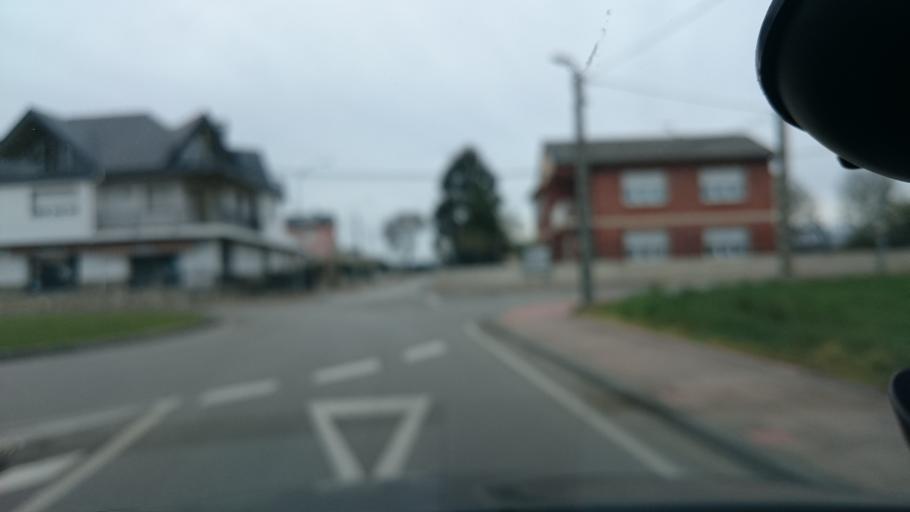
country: ES
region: Castille and Leon
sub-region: Provincia de Leon
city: Carracedelo
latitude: 42.5575
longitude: -6.7291
